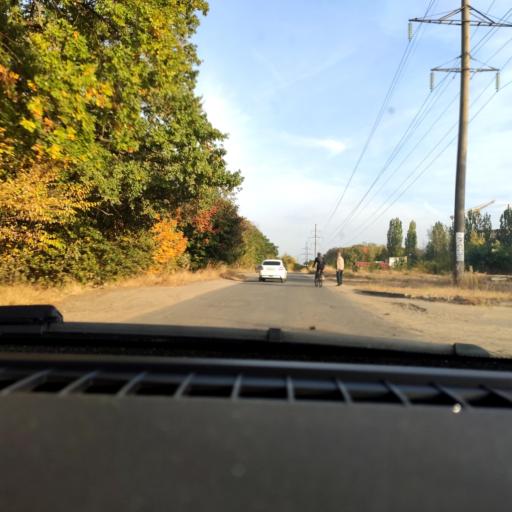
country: RU
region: Voronezj
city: Podgornoye
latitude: 51.7307
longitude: 39.2078
